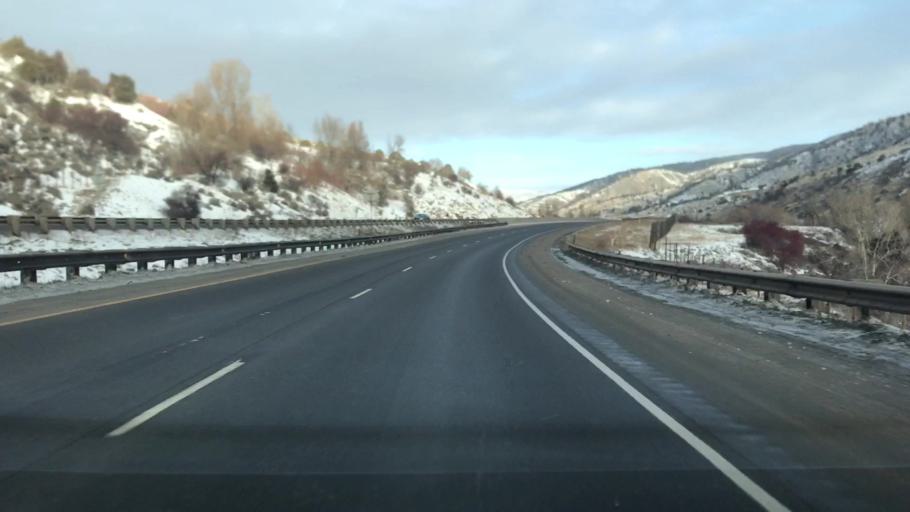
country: US
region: Colorado
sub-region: Eagle County
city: Edwards
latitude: 39.6753
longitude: -106.6475
